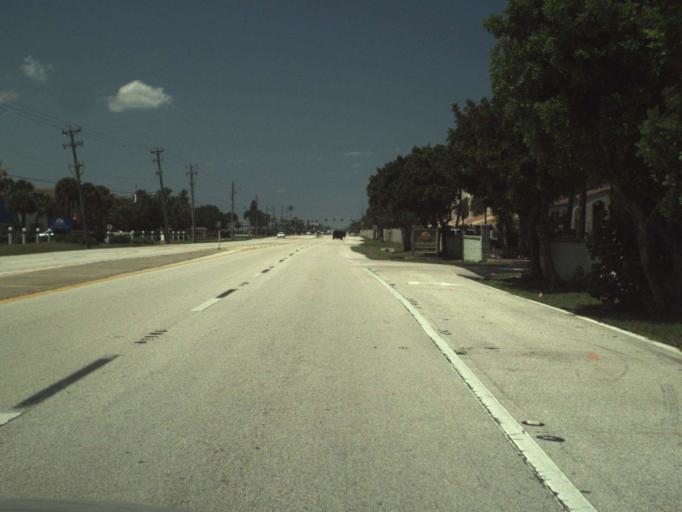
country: US
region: Florida
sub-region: Brevard County
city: South Patrick Shores
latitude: 28.2088
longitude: -80.5972
